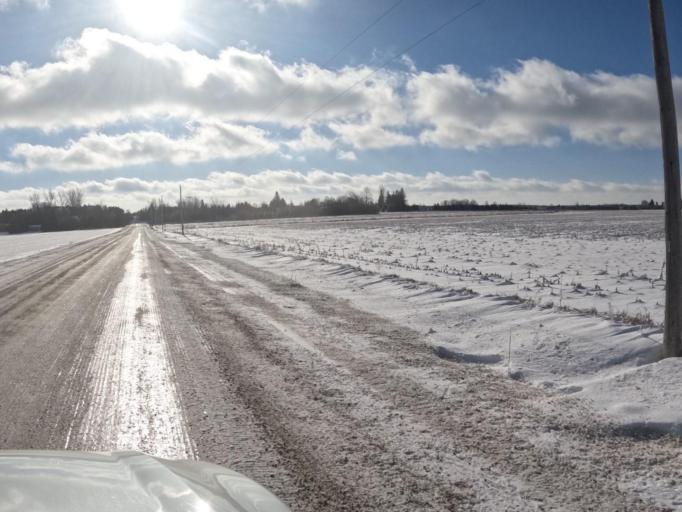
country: CA
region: Ontario
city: Shelburne
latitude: 43.9859
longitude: -80.4064
